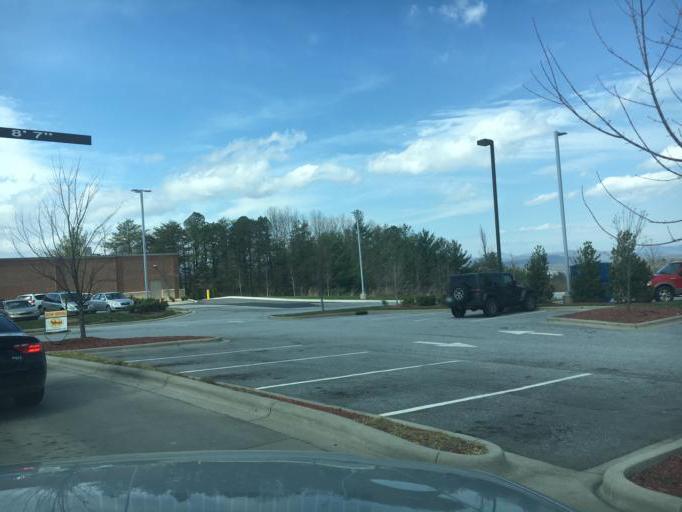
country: US
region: North Carolina
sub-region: Buncombe County
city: Royal Pines
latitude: 35.4510
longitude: -82.5281
